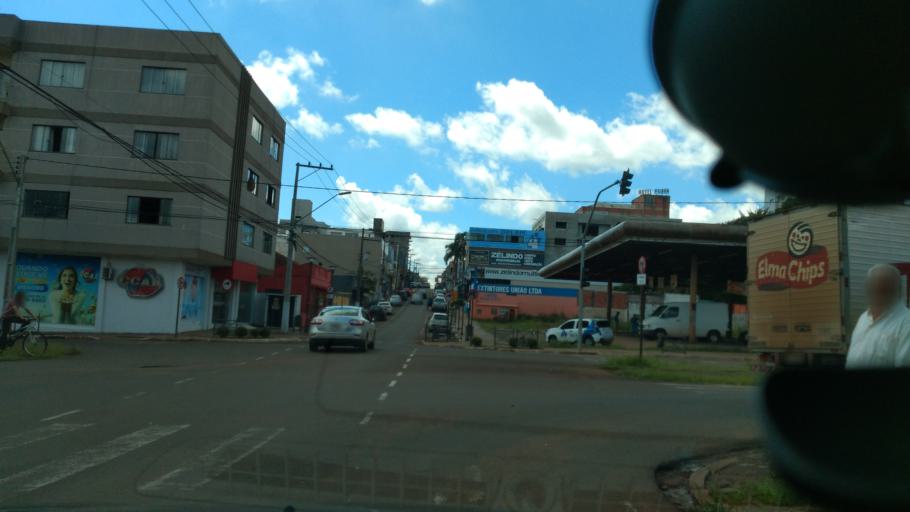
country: BR
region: Parana
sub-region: Guarapuava
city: Guarapuava
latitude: -25.3889
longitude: -51.4762
